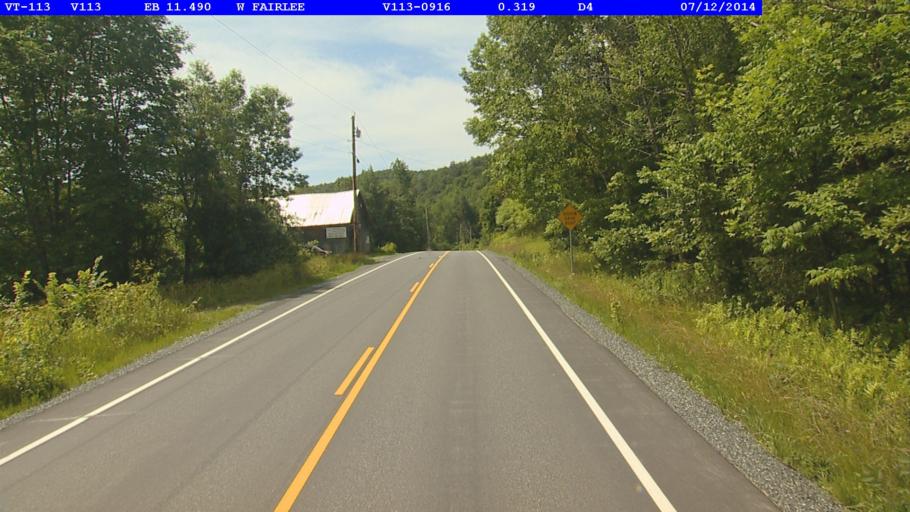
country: US
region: New Hampshire
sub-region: Grafton County
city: Orford
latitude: 43.9319
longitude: -72.2678
